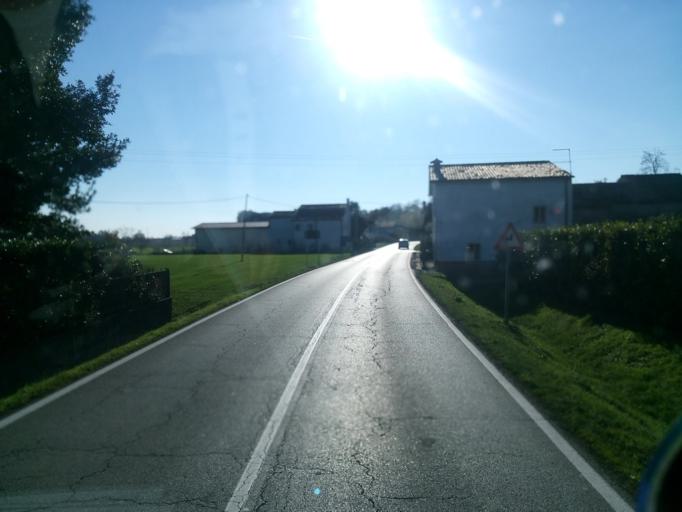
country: IT
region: Veneto
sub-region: Provincia di Vicenza
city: Sossano
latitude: 45.3733
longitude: 11.5249
